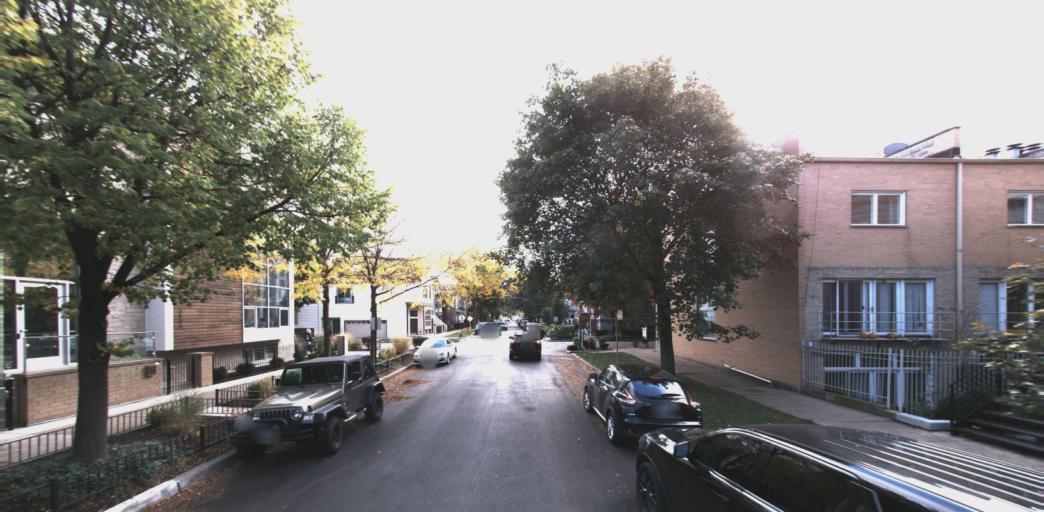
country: US
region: Illinois
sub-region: Cook County
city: Chicago
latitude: 41.9273
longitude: -87.6658
